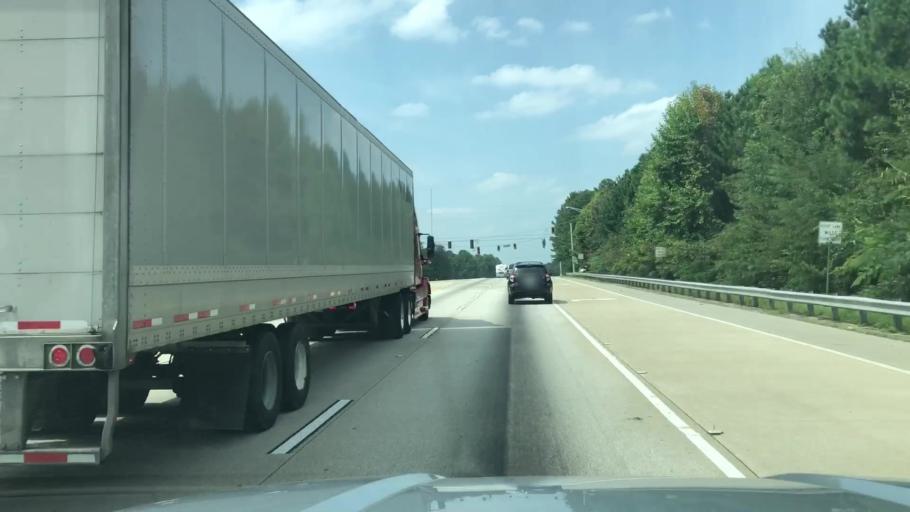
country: US
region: Georgia
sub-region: Douglas County
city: Lithia Springs
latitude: 33.8067
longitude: -84.6533
